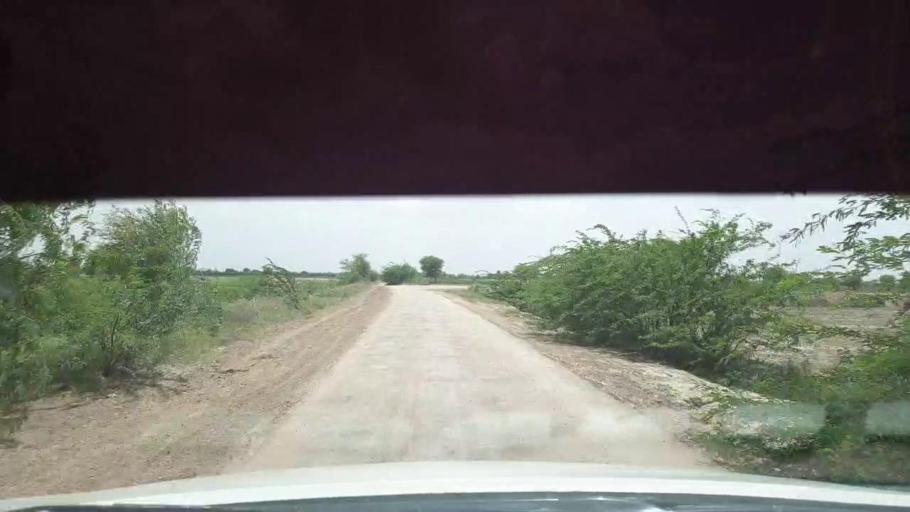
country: PK
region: Sindh
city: Kadhan
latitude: 24.5270
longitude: 69.0951
